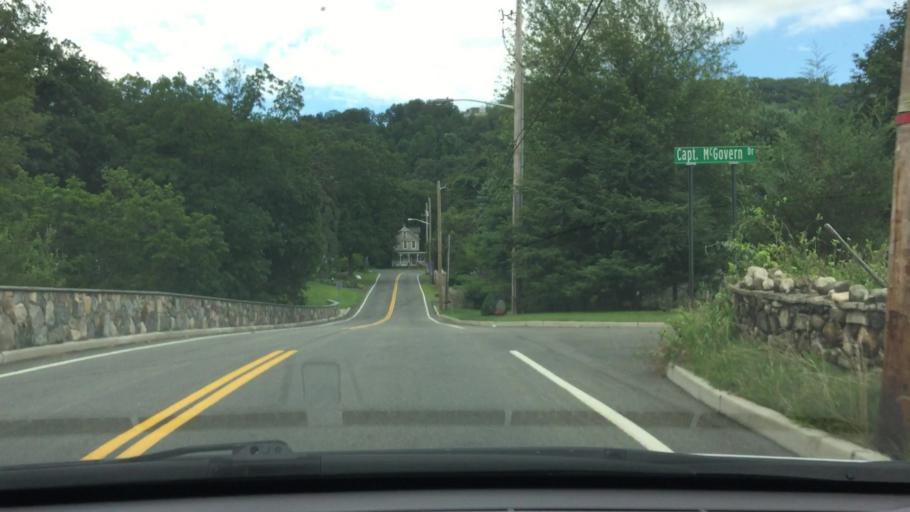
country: US
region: New York
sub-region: Rockland County
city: Stony Point
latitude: 41.2266
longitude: -74.0044
